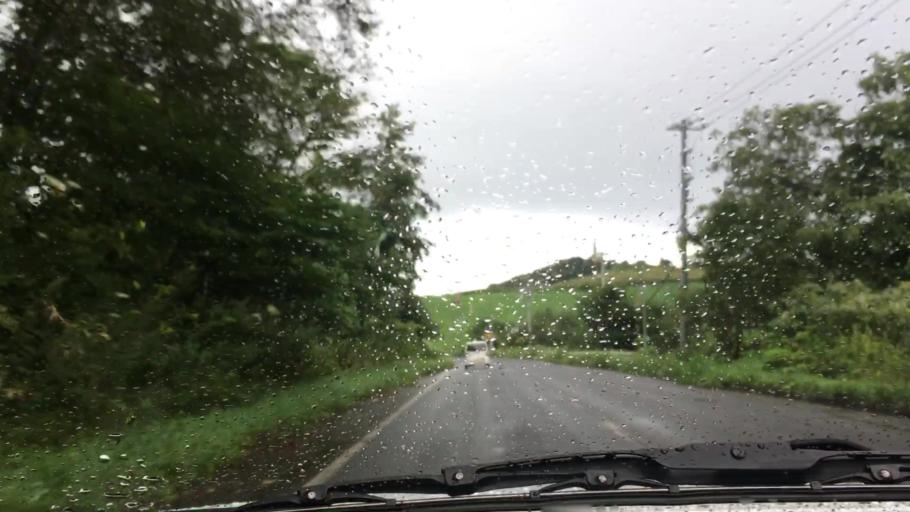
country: JP
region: Hokkaido
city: Niseko Town
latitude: 42.5958
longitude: 140.7212
